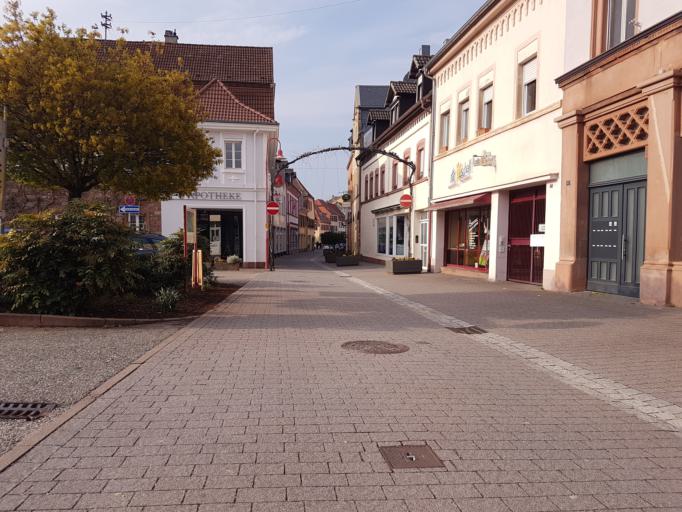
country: DE
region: Rheinland-Pfalz
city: Edenkoben
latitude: 49.2791
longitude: 8.1274
